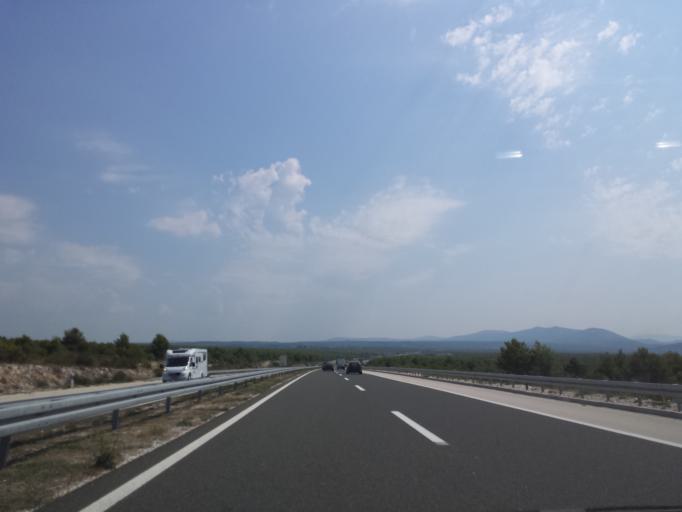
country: HR
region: Sibensko-Kniniska
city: Zaton
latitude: 43.8488
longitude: 15.8673
